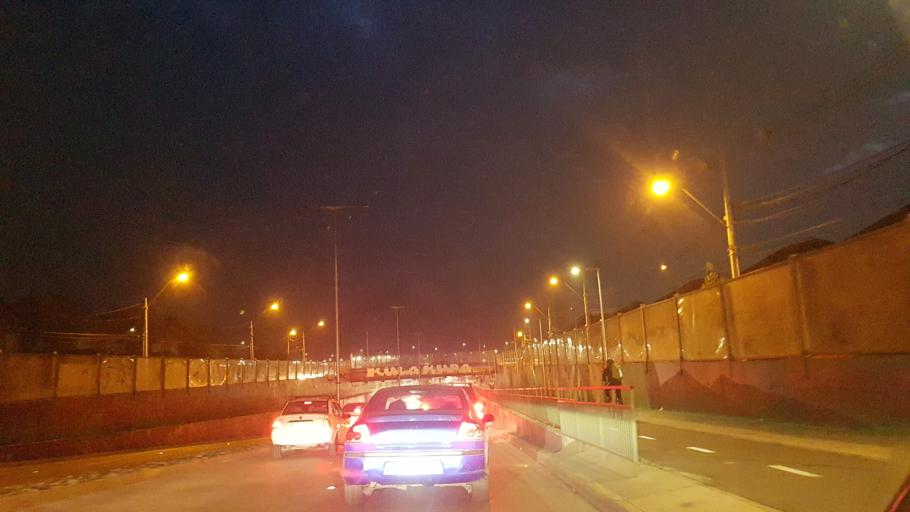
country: CL
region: Santiago Metropolitan
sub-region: Provincia de Santiago
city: Lo Prado
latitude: -33.3567
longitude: -70.7140
